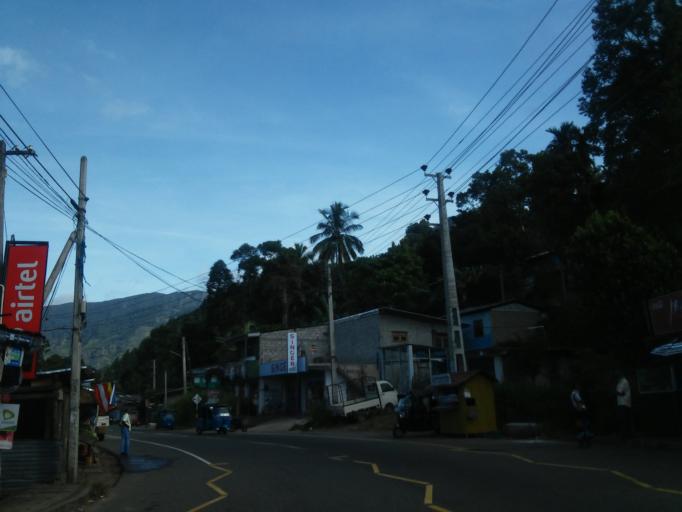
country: LK
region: Uva
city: Haputale
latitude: 6.7606
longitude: 80.8806
